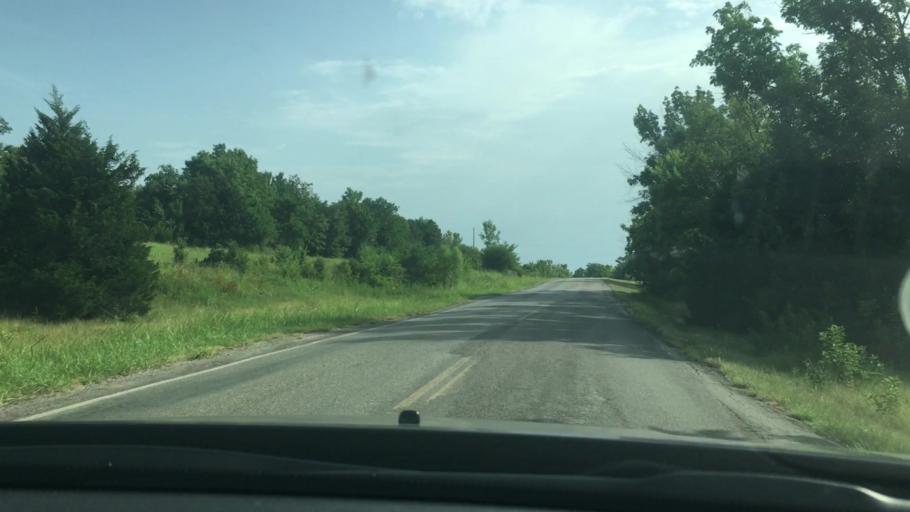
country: US
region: Oklahoma
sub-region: Pontotoc County
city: Byng
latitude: 34.8679
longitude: -96.5986
